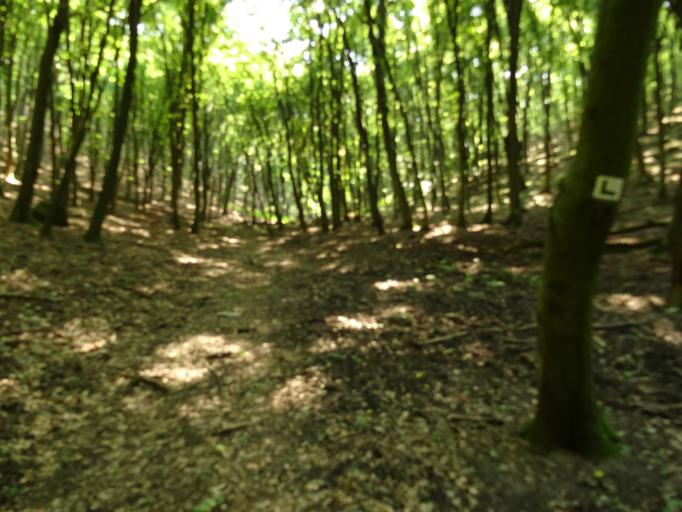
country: HU
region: Borsod-Abauj-Zemplen
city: Szendro
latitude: 48.4727
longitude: 20.7173
